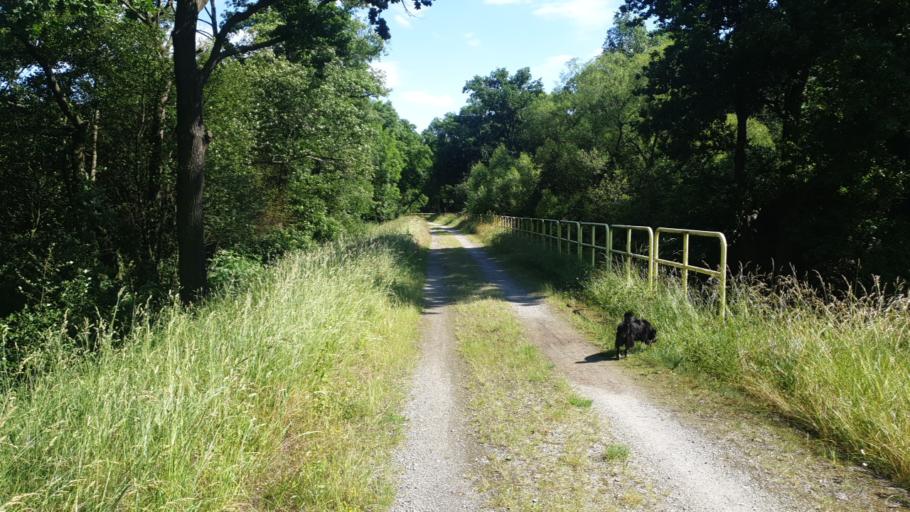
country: PL
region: Lower Silesian Voivodeship
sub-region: Powiat wroclawski
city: Radwanice
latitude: 51.0864
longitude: 17.1171
